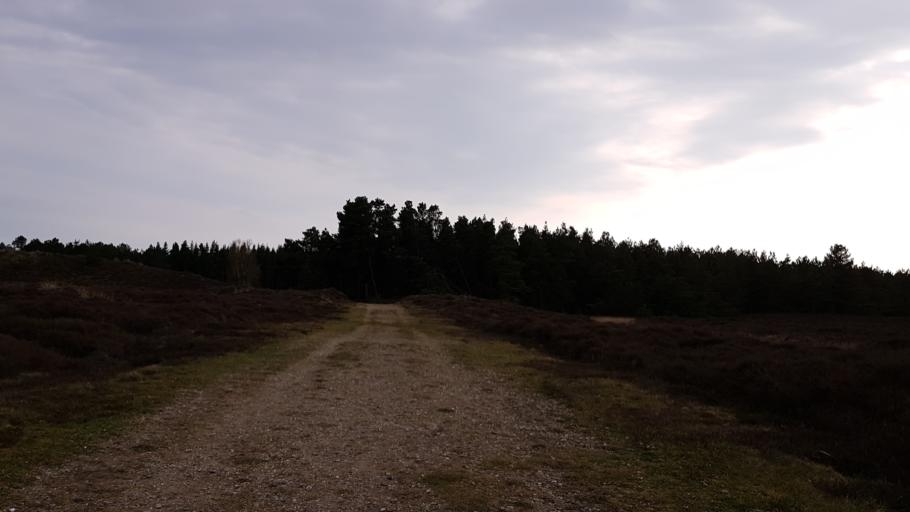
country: DE
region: Schleswig-Holstein
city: List
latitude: 55.1548
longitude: 8.5321
